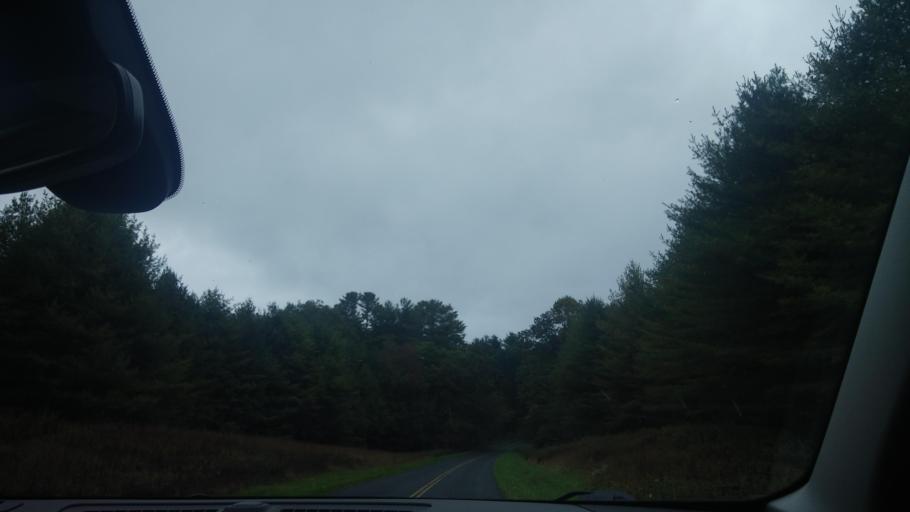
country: US
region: Virginia
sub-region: City of Galax
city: Galax
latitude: 36.5896
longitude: -80.8540
